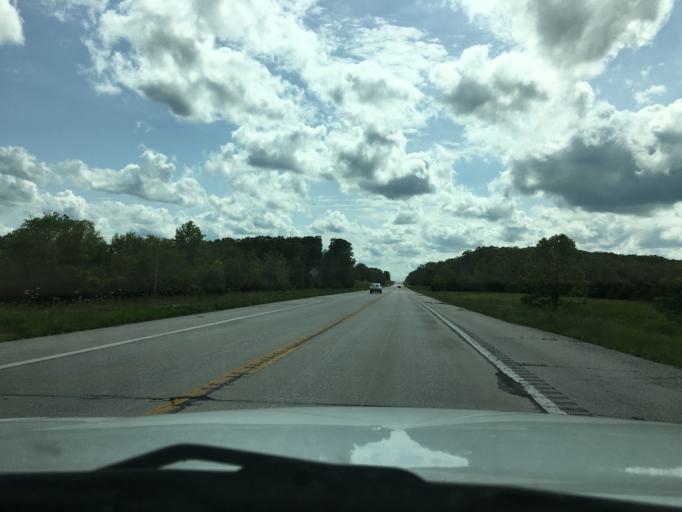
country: US
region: Missouri
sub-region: Franklin County
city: Gerald
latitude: 38.4227
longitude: -91.2810
